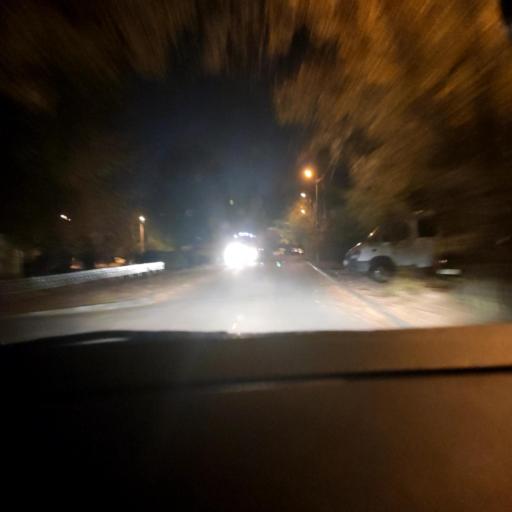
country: RU
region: Voronezj
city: Voronezh
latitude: 51.6559
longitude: 39.1553
